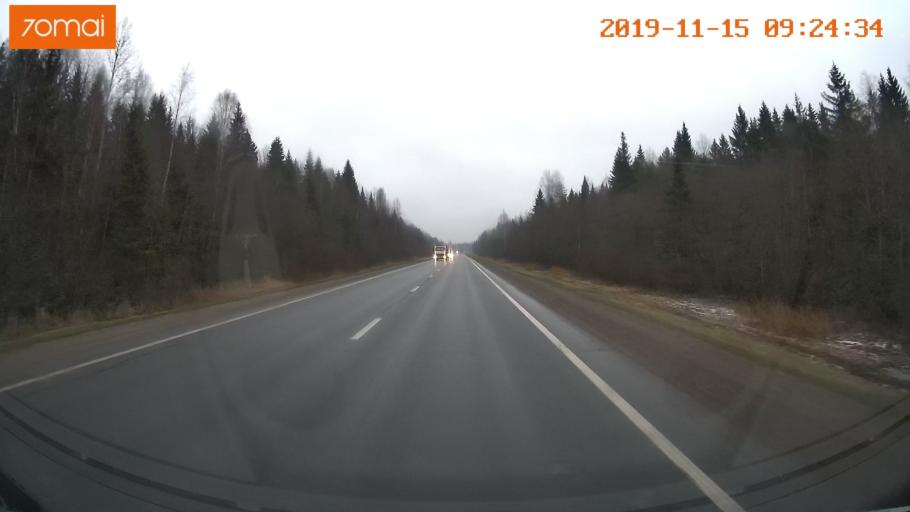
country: RU
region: Vologda
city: Tonshalovo
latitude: 59.3048
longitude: 38.1420
